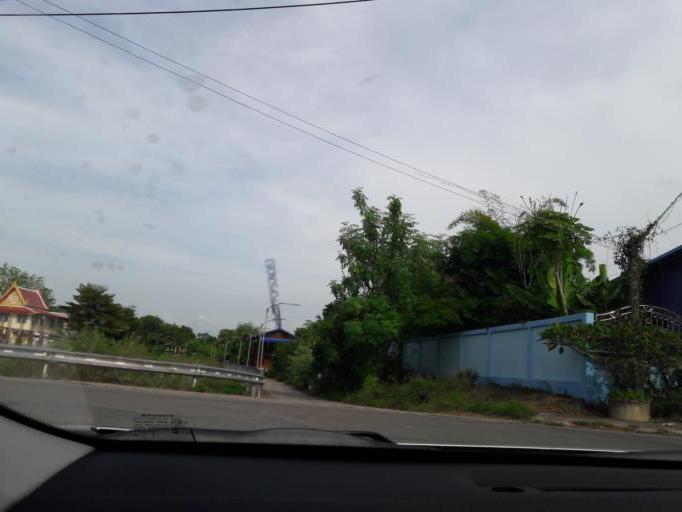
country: TH
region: Ang Thong
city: Ang Thong
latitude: 14.5881
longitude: 100.4467
